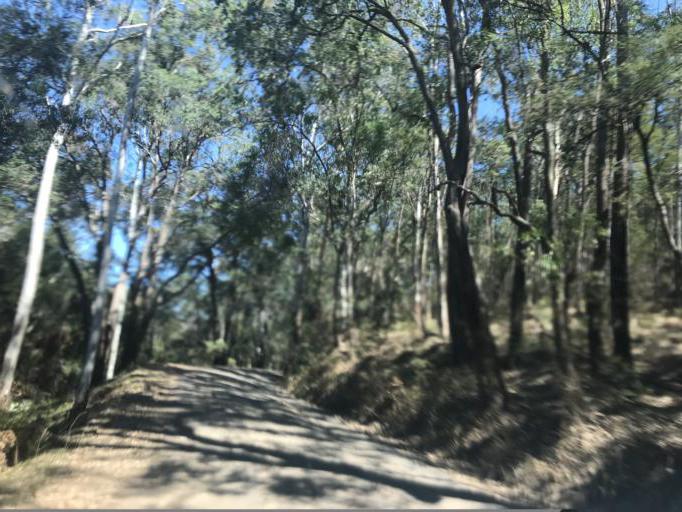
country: AU
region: New South Wales
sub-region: Wyong Shire
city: Little Jilliby
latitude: -33.1976
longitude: 151.0042
